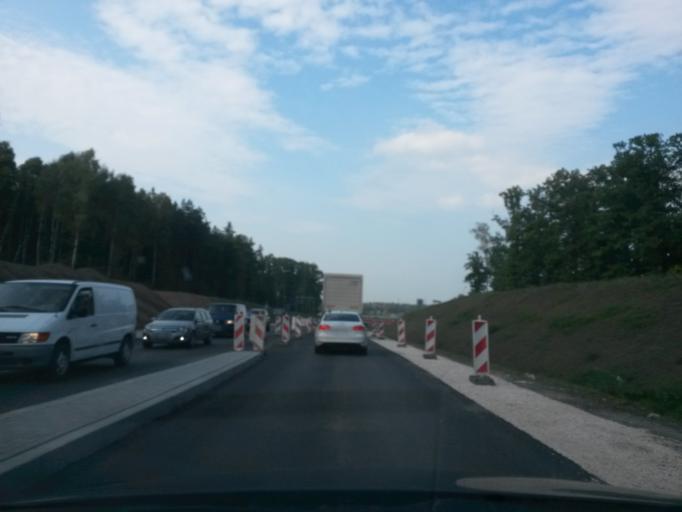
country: PL
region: Lesser Poland Voivodeship
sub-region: Powiat brzeski
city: Brzesko
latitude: 49.9850
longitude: 20.5931
